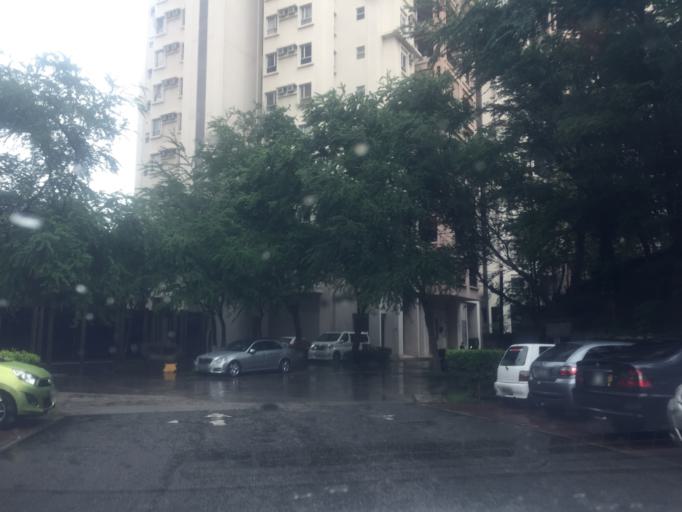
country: MY
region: Kuala Lumpur
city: Kuala Lumpur
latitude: 3.1758
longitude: 101.7337
